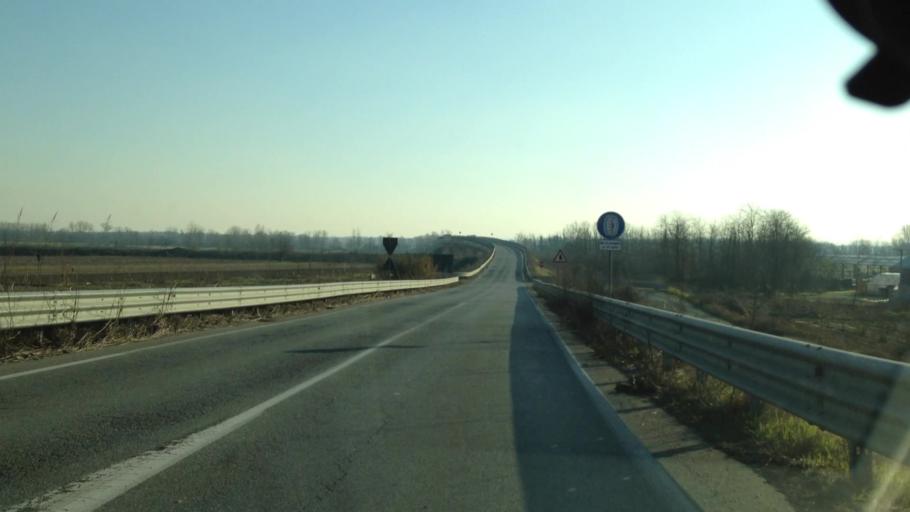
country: IT
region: Piedmont
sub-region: Provincia di Alessandria
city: Felizzano
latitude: 44.9011
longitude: 8.4491
